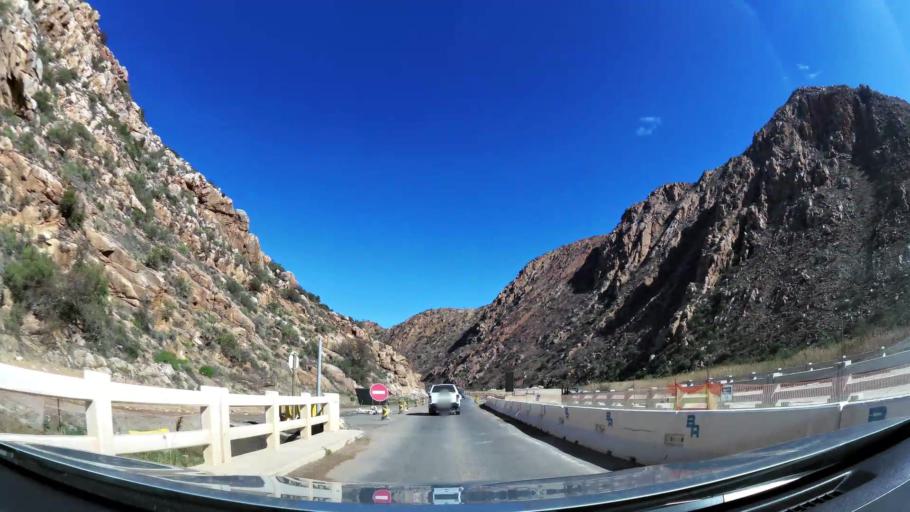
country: ZA
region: Western Cape
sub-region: Cape Winelands District Municipality
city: Ashton
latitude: -33.7938
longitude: 20.1056
